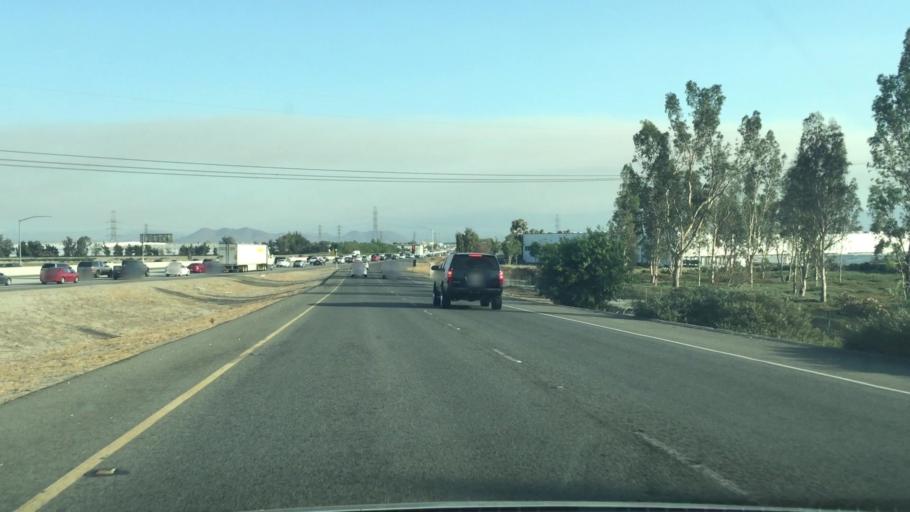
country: US
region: California
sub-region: Riverside County
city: Mira Loma
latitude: 34.0461
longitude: -117.5509
